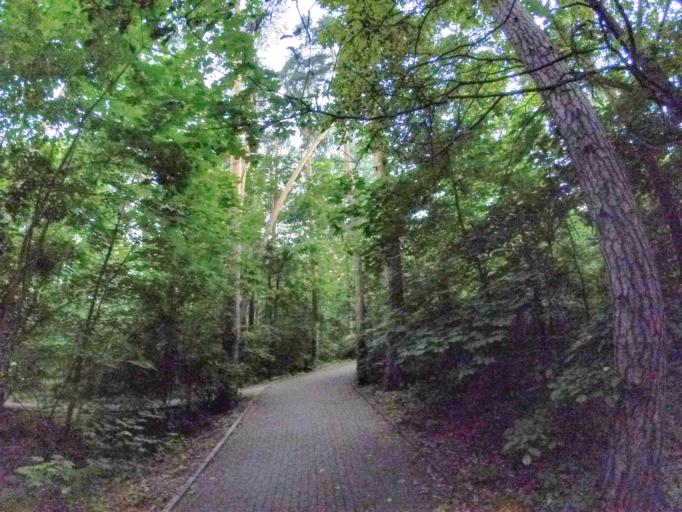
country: RU
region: Moscow
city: Shchukino
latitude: 55.7808
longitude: 37.4288
